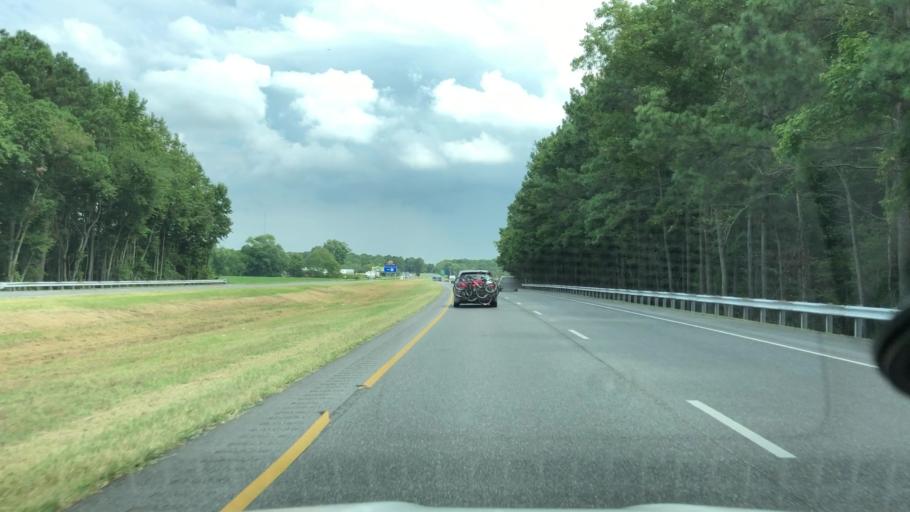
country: US
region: Maryland
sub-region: Worcester County
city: Pocomoke City
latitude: 38.0817
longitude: -75.5971
